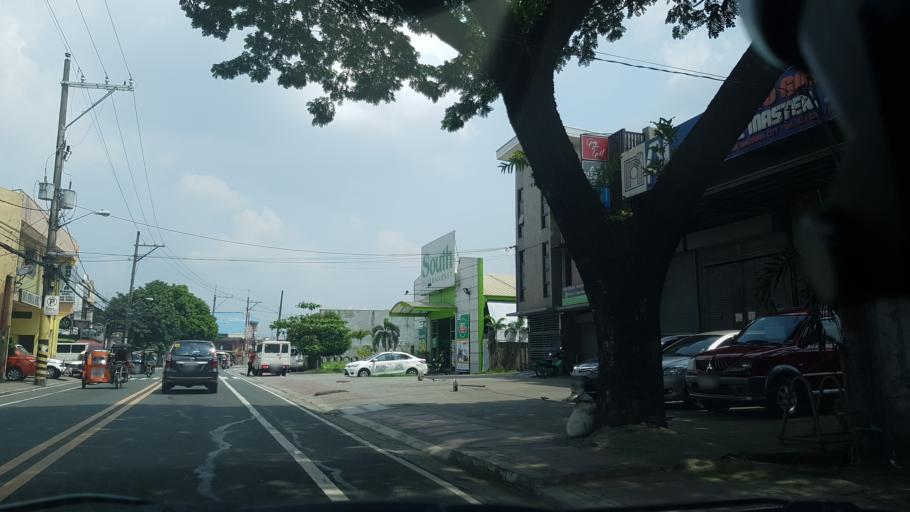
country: PH
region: Metro Manila
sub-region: Marikina
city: Calumpang
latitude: 14.6467
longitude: 121.0968
